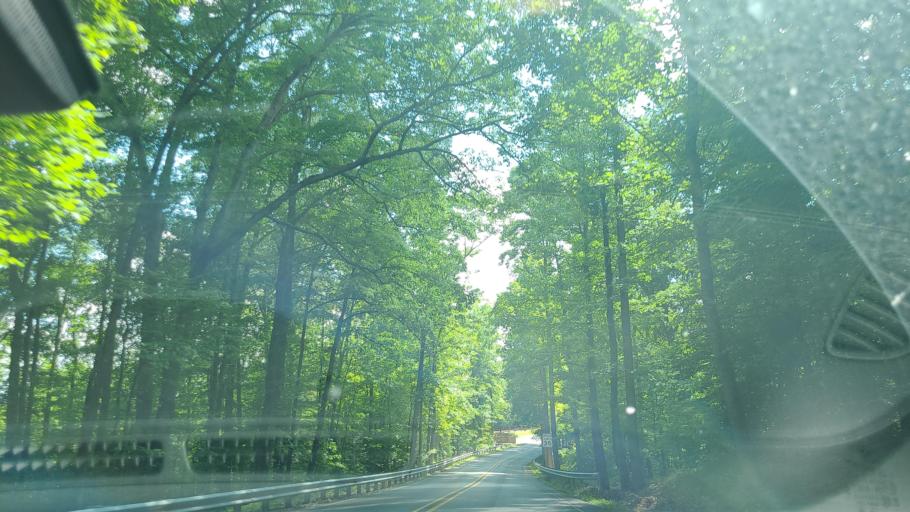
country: US
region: Kentucky
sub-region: McCreary County
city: Whitley City
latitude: 36.8420
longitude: -84.3340
